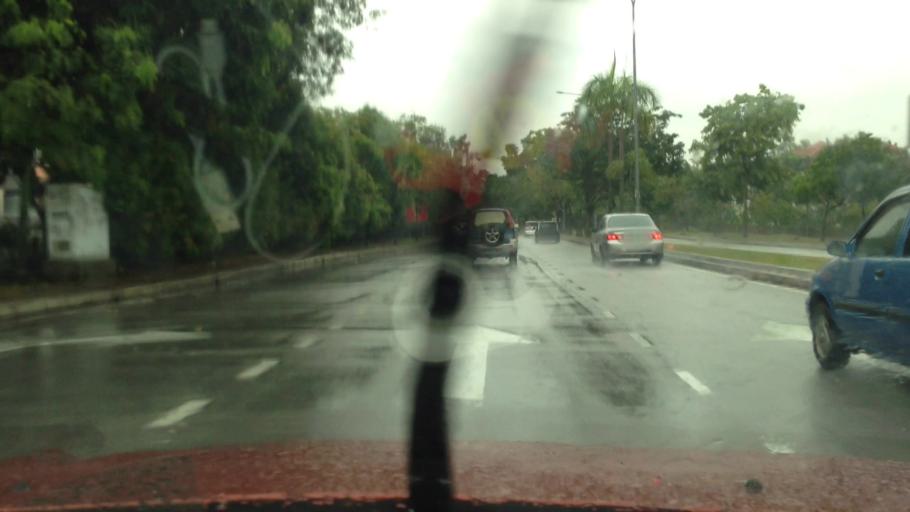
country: MY
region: Selangor
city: Subang Jaya
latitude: 3.0573
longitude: 101.5715
